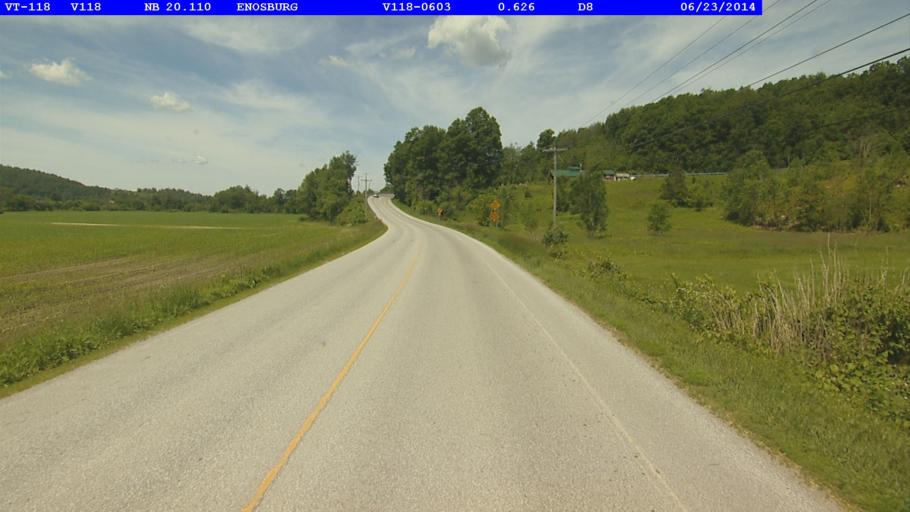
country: US
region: Vermont
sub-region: Franklin County
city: Richford
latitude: 44.9276
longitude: -72.6808
